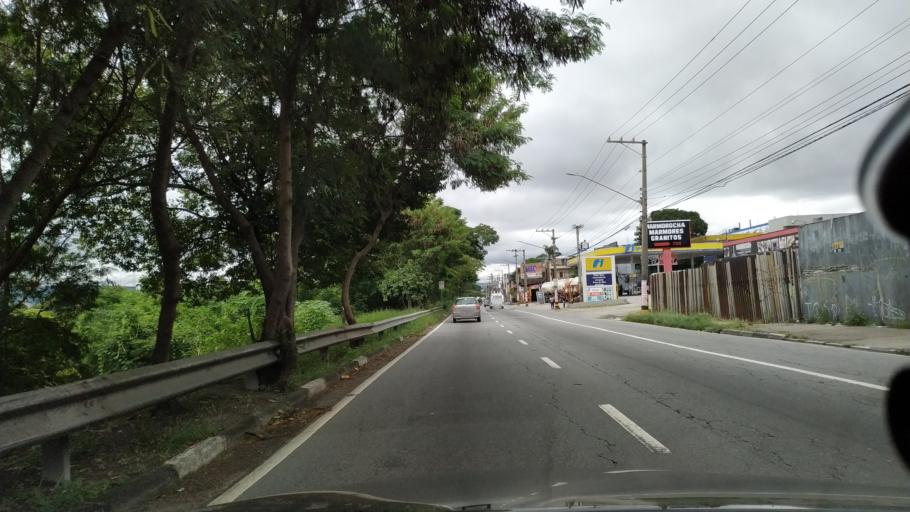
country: BR
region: Sao Paulo
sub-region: Osasco
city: Osasco
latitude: -23.5217
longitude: -46.7821
